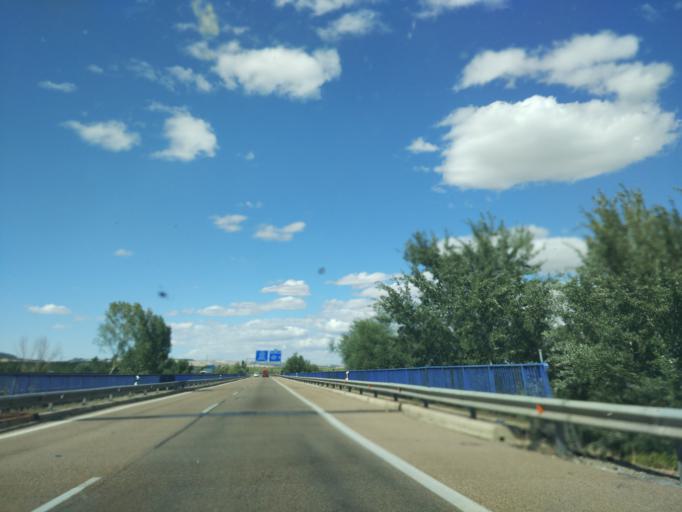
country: ES
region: Castille and Leon
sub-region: Provincia de Valladolid
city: Tordesillas
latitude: 41.4891
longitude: -4.9845
